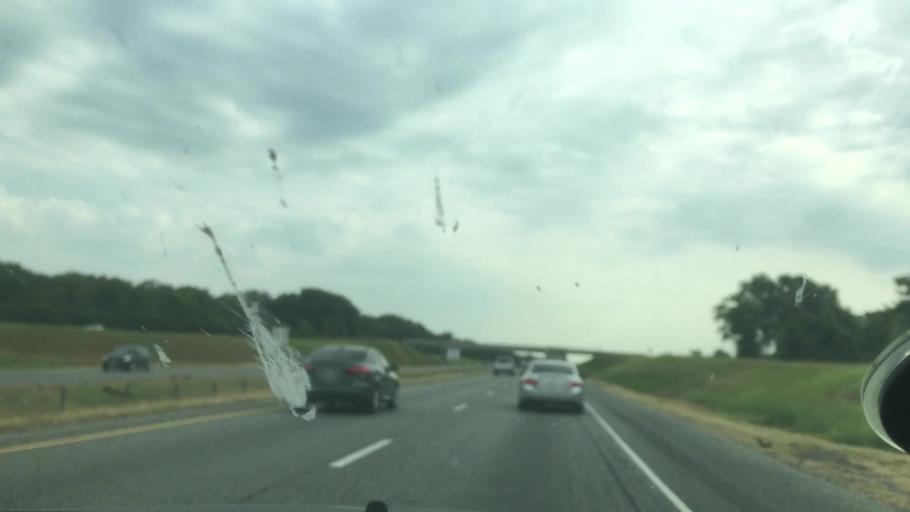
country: US
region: Oklahoma
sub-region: Bryan County
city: Colbert
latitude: 33.8290
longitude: -96.5283
